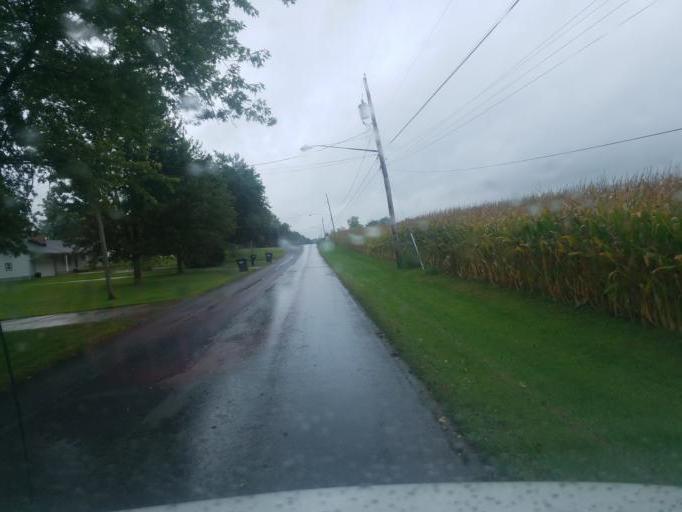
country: US
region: Ohio
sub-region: Wayne County
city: Creston
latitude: 40.9775
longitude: -81.9093
